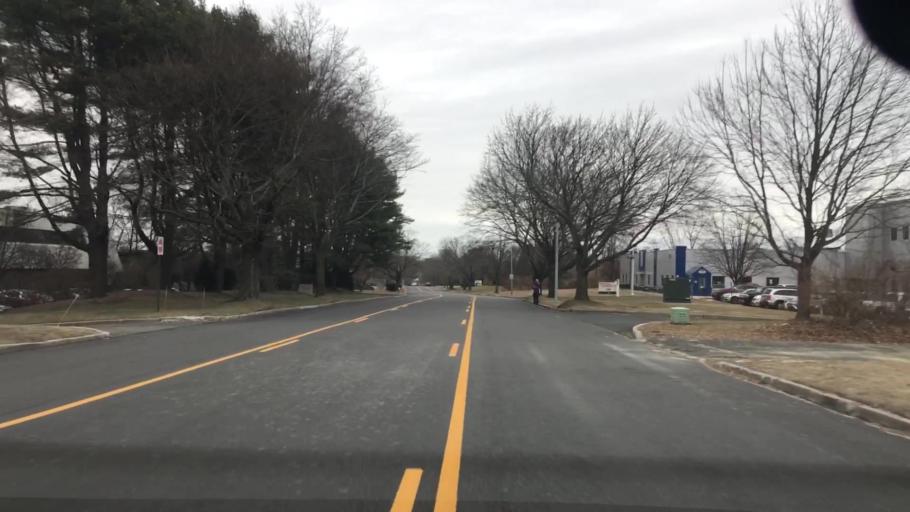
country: US
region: New York
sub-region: Suffolk County
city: Brentwood
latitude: 40.8134
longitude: -73.2401
